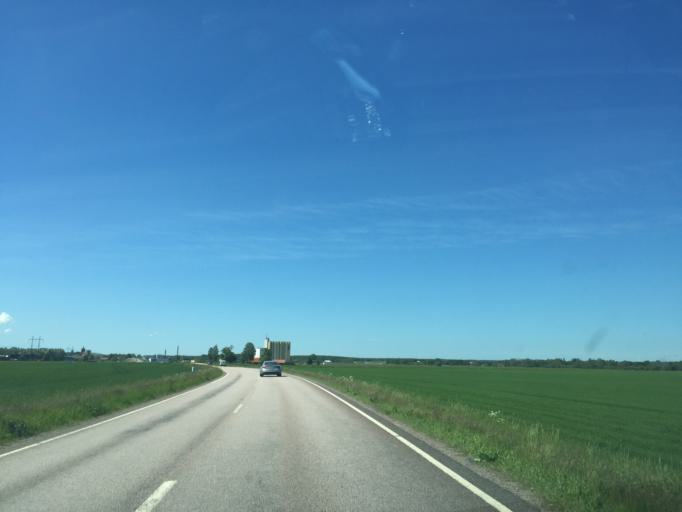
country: SE
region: OEstergoetland
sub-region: Mjolby Kommun
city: Mjolby
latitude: 58.3902
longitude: 15.1211
